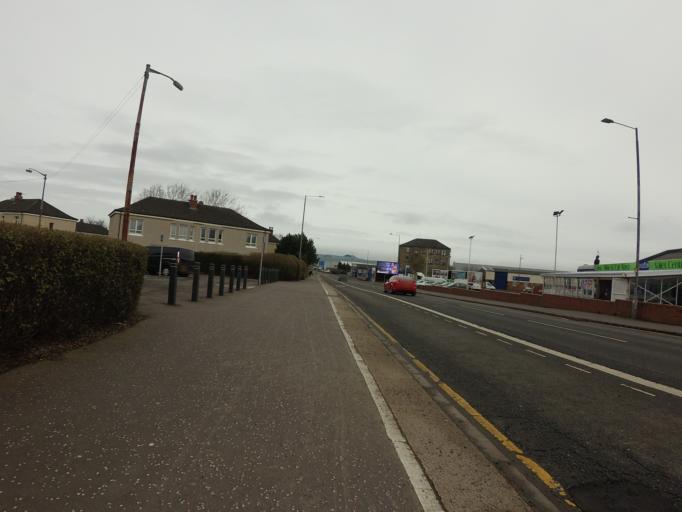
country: GB
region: Scotland
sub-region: Glasgow City
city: Glasgow
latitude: 55.8335
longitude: -4.2487
